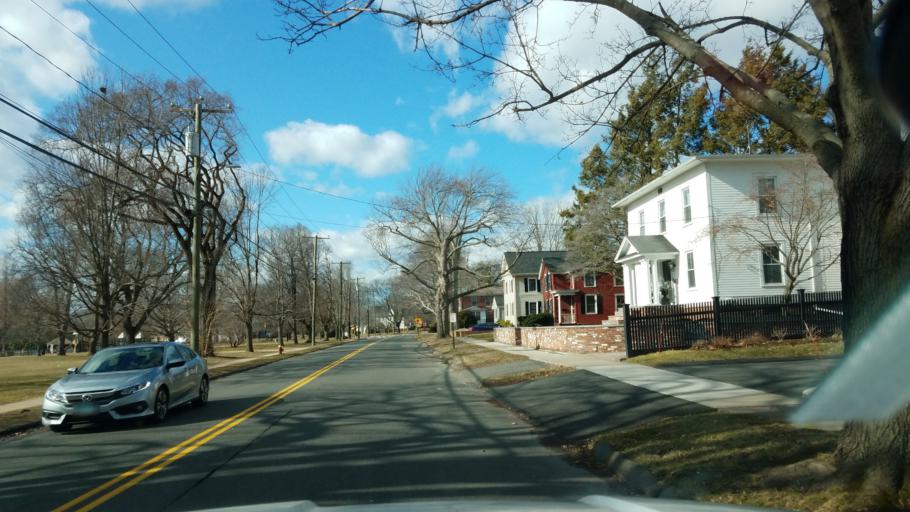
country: US
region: Connecticut
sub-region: Hartford County
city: Wethersfield
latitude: 41.7171
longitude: -72.6583
